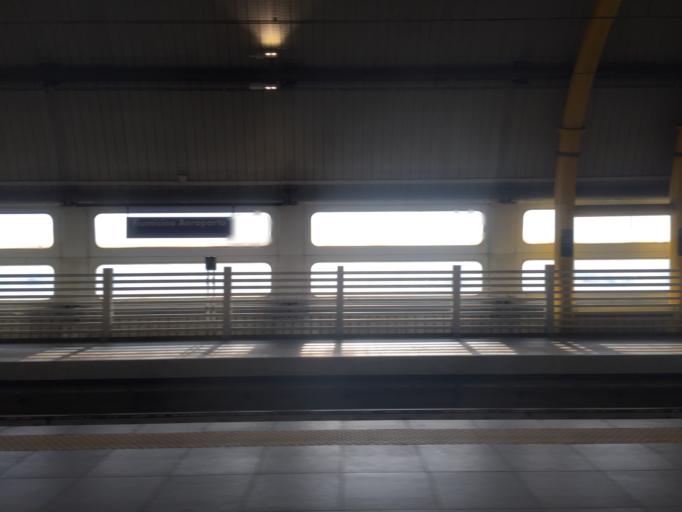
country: IT
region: Latium
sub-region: Citta metropolitana di Roma Capitale
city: Fiumicino-Isola Sacra
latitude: 41.7926
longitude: 12.2527
